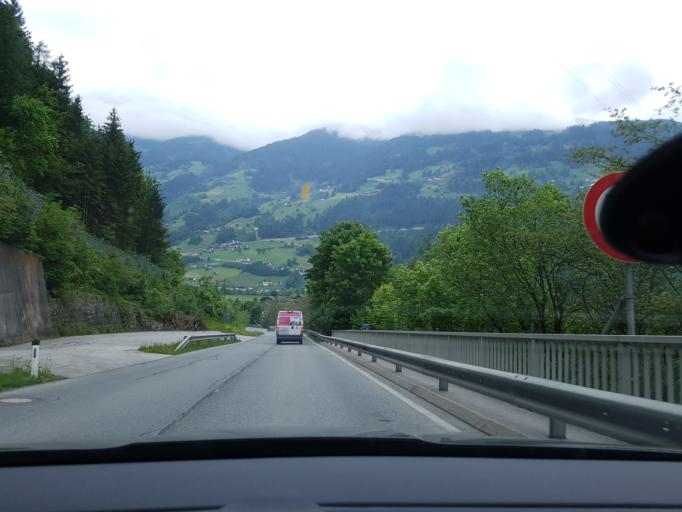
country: AT
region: Tyrol
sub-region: Politischer Bezirk Schwaz
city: Zell am Ziller
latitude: 47.2256
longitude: 11.8902
